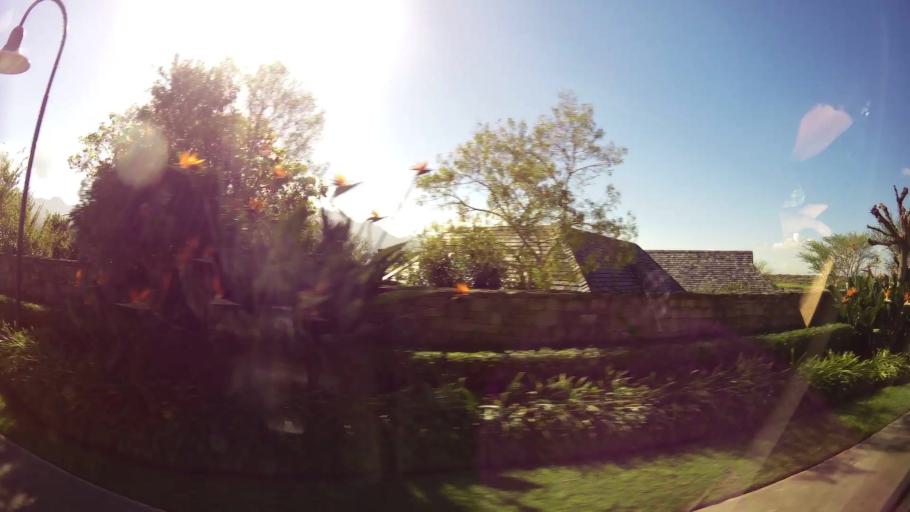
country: ZA
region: Western Cape
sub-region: Eden District Municipality
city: George
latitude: -33.9659
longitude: 22.4074
